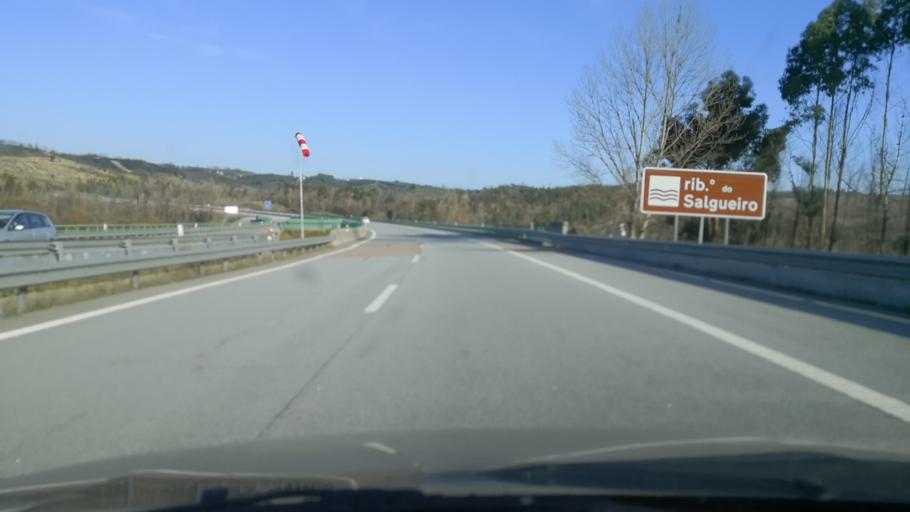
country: PT
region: Portalegre
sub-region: Gaviao
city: Gaviao
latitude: 39.5324
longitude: -7.9044
